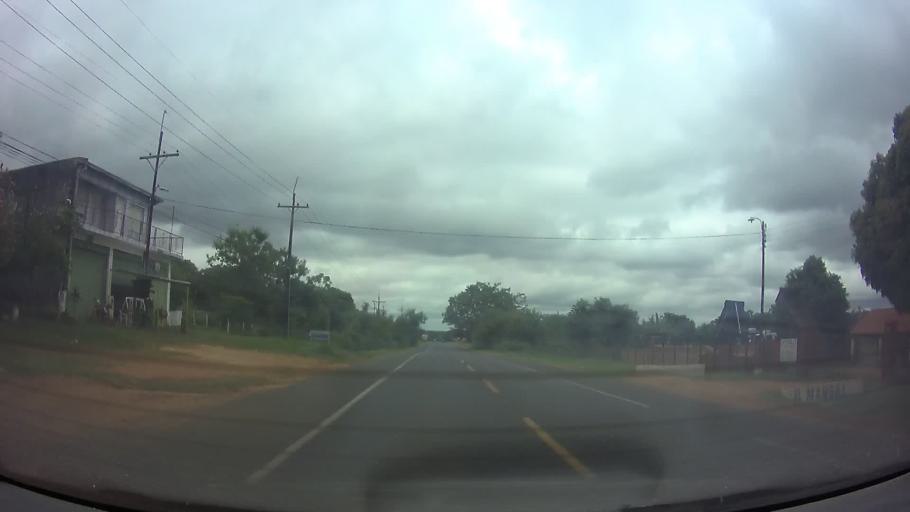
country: PY
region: Central
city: Guarambare
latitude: -25.5014
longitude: -57.4982
